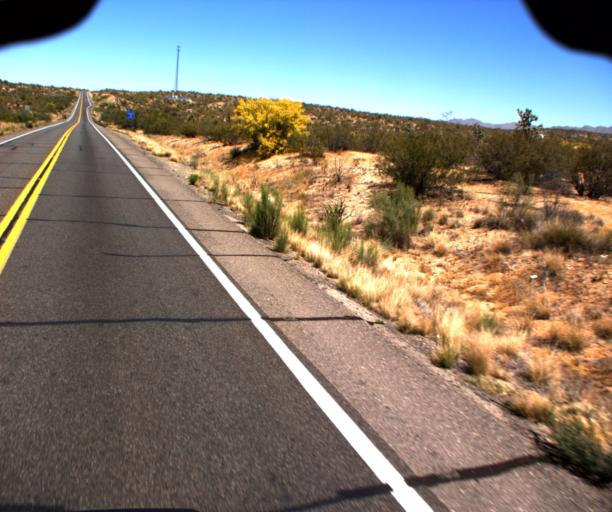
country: US
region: Arizona
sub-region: Yavapai County
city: Congress
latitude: 34.2094
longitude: -113.0653
